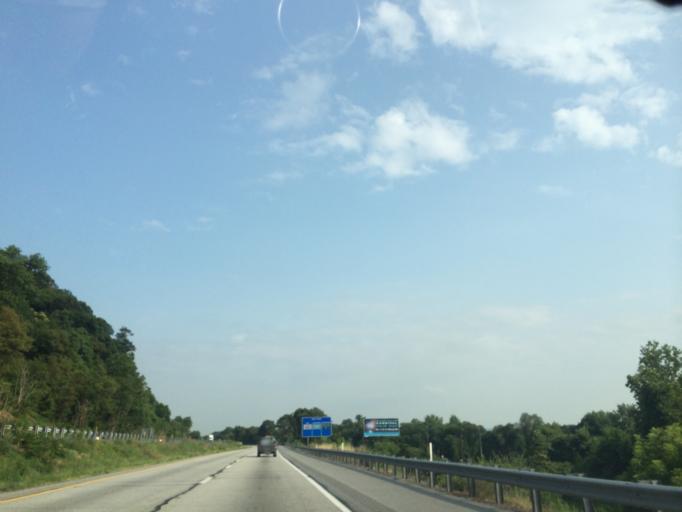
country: US
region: Pennsylvania
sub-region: Perry County
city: Marysville
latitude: 40.3367
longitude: -76.9027
